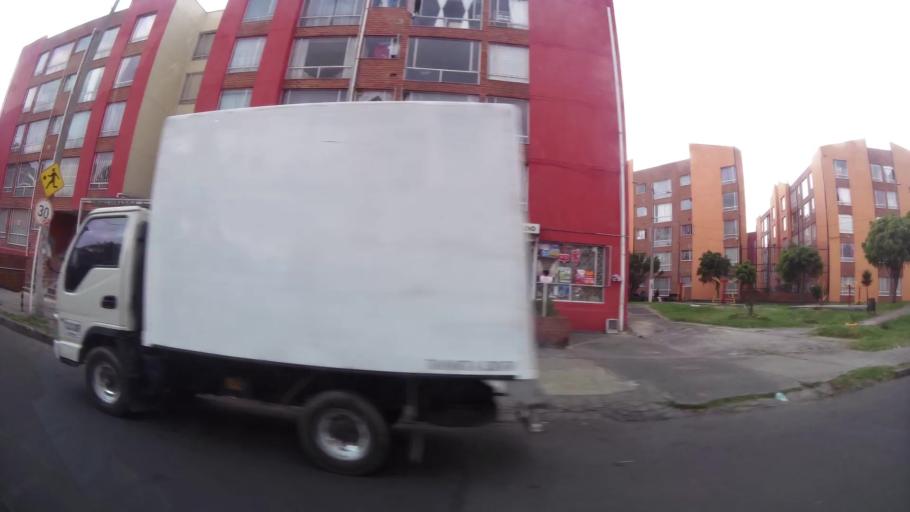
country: CO
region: Bogota D.C.
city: Bogota
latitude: 4.5796
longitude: -74.0895
